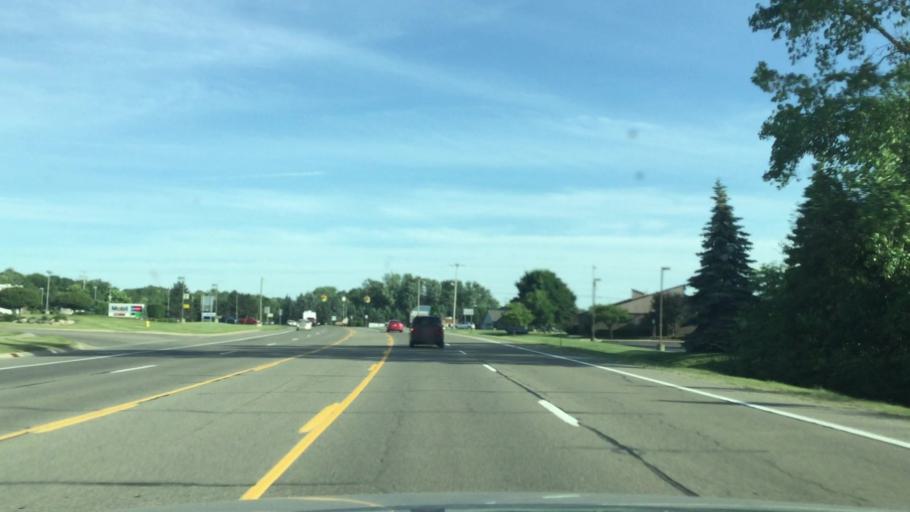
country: US
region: Michigan
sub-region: Genesee County
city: Davison
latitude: 43.0071
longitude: -83.5168
